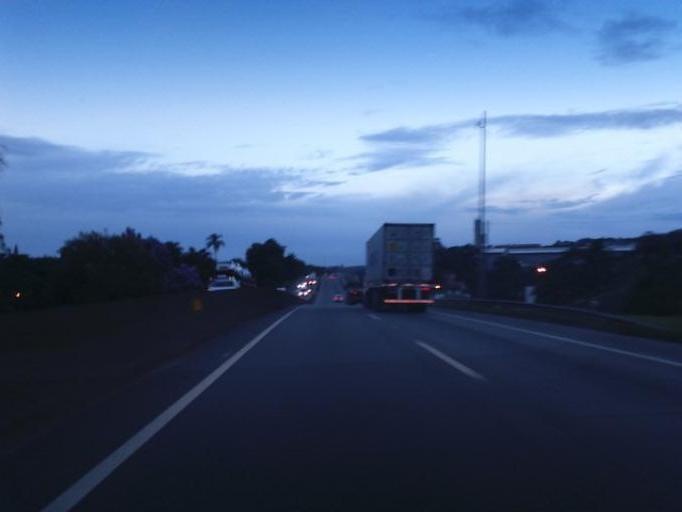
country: BR
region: Santa Catarina
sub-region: Joinville
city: Joinville
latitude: -26.3321
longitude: -48.8615
